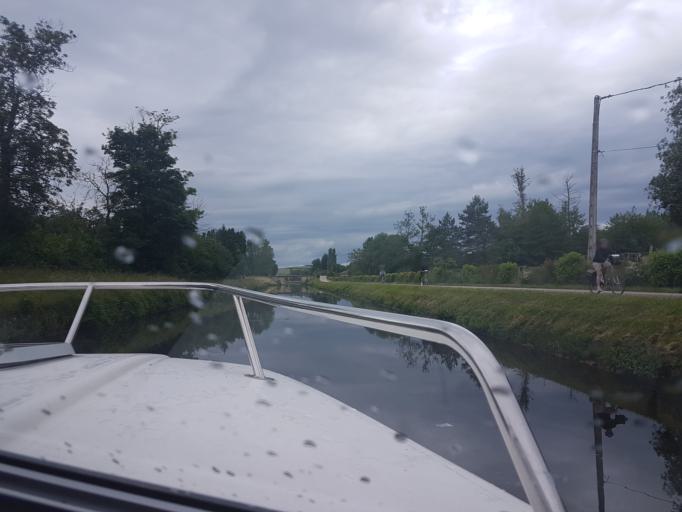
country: FR
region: Bourgogne
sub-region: Departement de l'Yonne
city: Saint-Bris-le-Vineux
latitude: 47.7085
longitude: 3.6364
